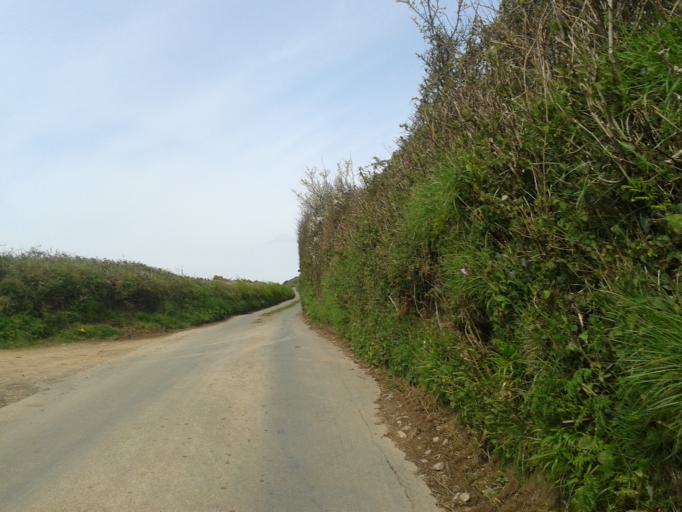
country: GB
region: England
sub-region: Devon
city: Braunton
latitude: 51.1421
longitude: -4.1858
